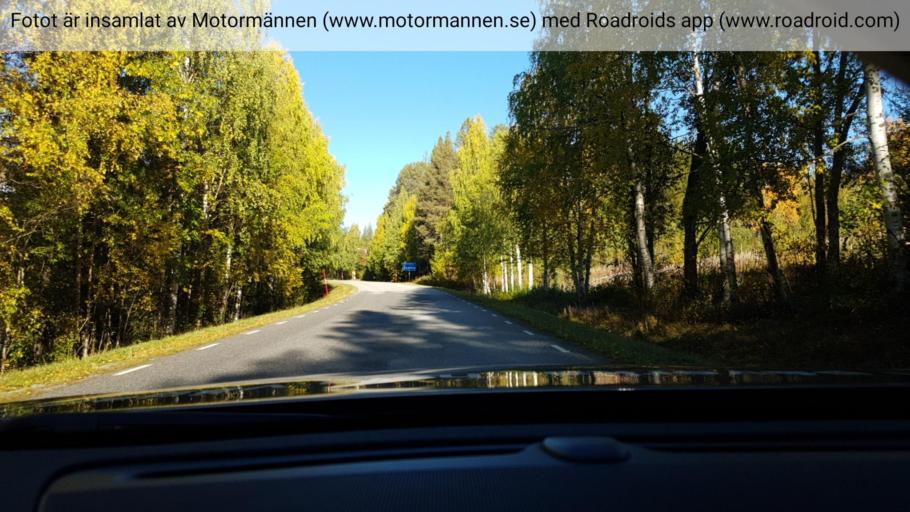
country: SE
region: Norrbotten
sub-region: Gallivare Kommun
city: Gaellivare
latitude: 66.4544
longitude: 20.6569
